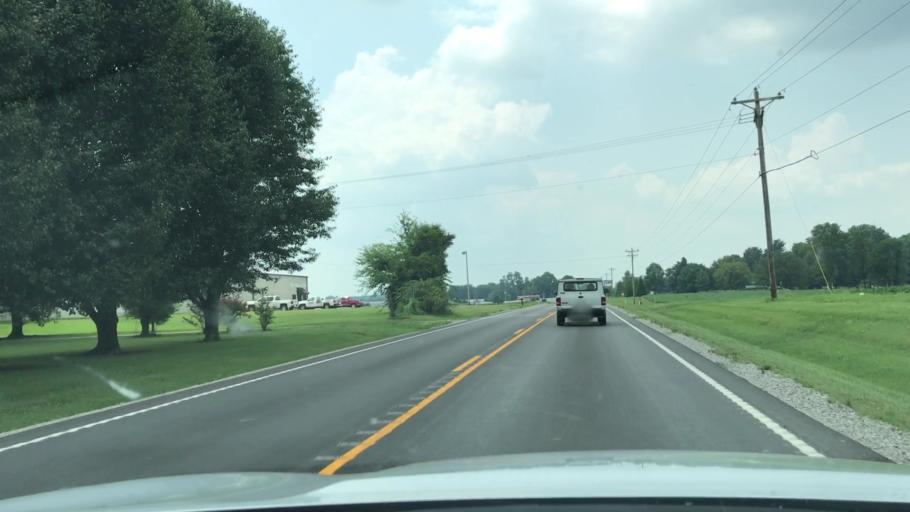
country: US
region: Kentucky
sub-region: Todd County
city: Guthrie
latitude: 36.6510
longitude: -87.1885
